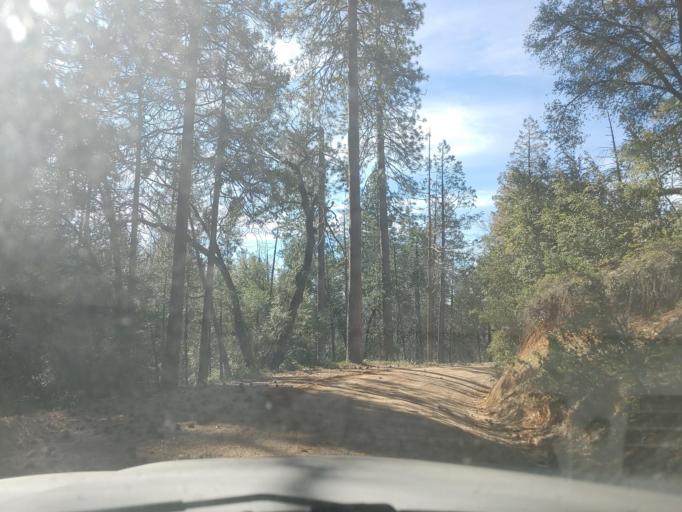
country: US
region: California
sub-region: Madera County
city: Ahwahnee
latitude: 37.4230
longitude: -119.6752
